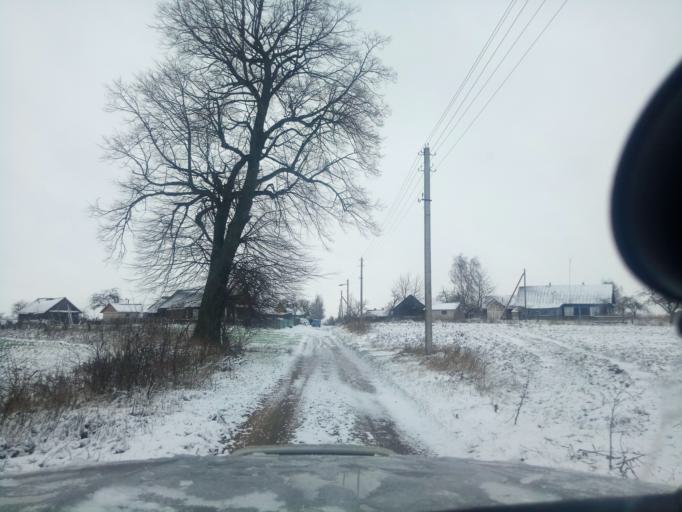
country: BY
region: Minsk
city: Klyetsk
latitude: 53.0214
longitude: 26.7121
